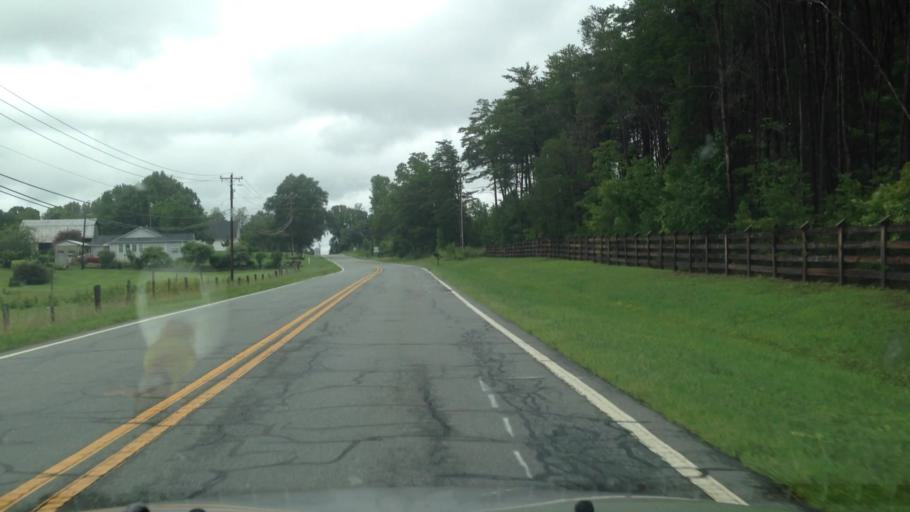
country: US
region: North Carolina
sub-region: Forsyth County
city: Kernersville
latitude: 36.1754
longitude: -80.0608
